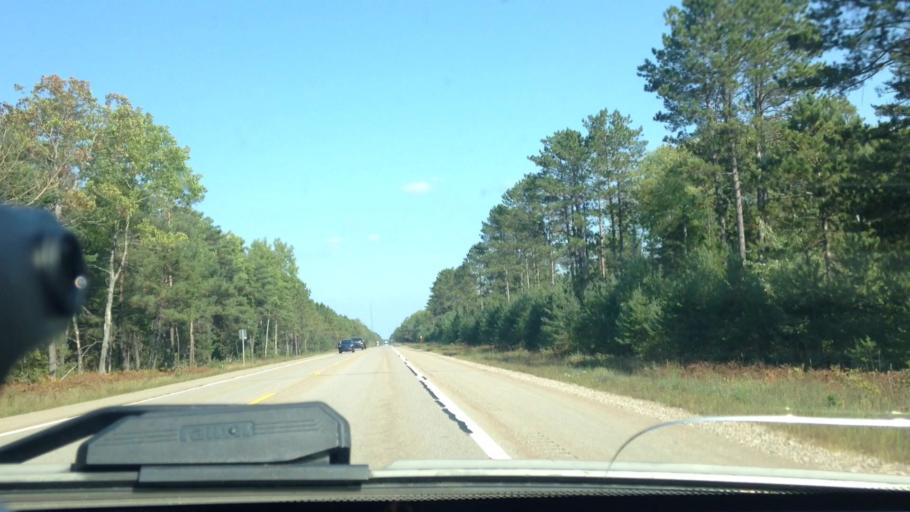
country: US
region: Michigan
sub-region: Chippewa County
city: Sault Ste. Marie
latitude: 46.3664
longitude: -84.7541
